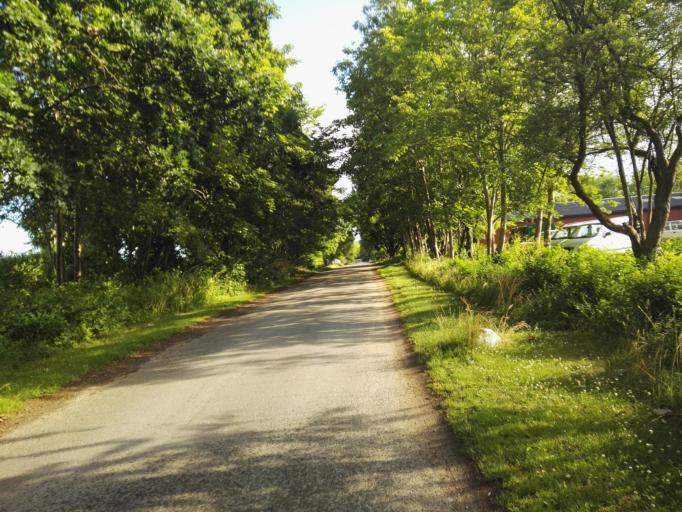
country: DK
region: Capital Region
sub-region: Ballerup Kommune
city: Ballerup
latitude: 55.7151
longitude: 12.3401
